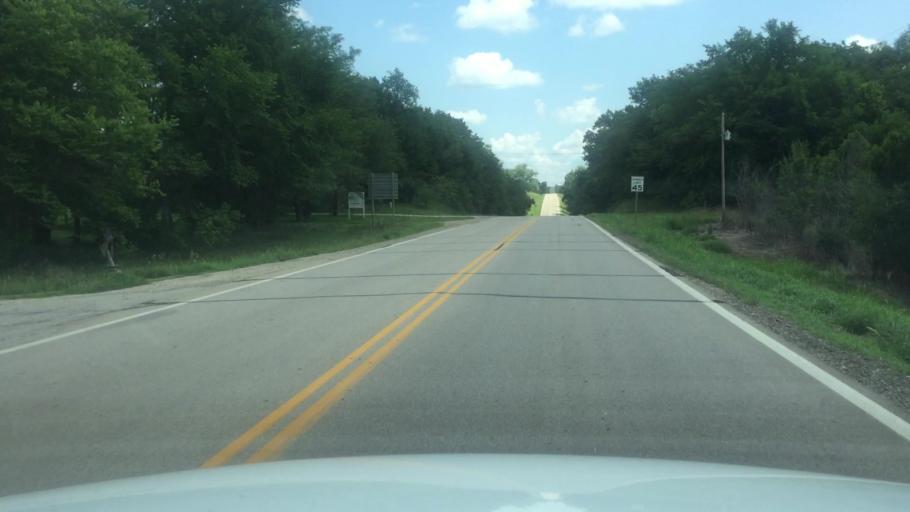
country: US
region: Kansas
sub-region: Brown County
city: Horton
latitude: 39.6674
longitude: -95.6388
